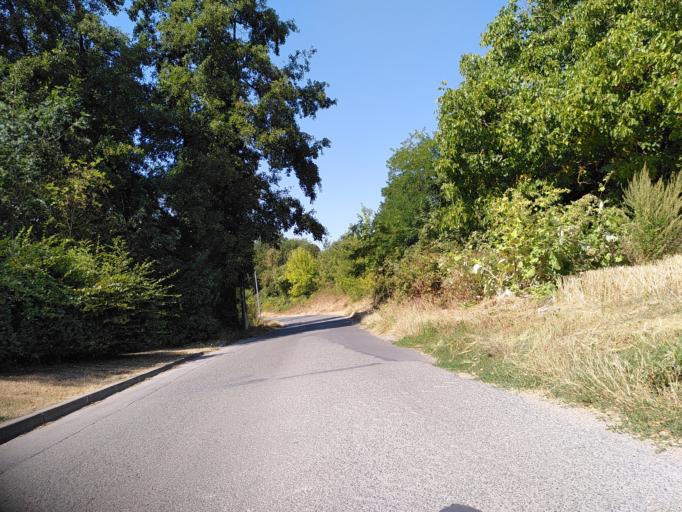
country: FR
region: Ile-de-France
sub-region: Departement de l'Essonne
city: Ollainville
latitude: 48.5859
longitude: 2.2161
